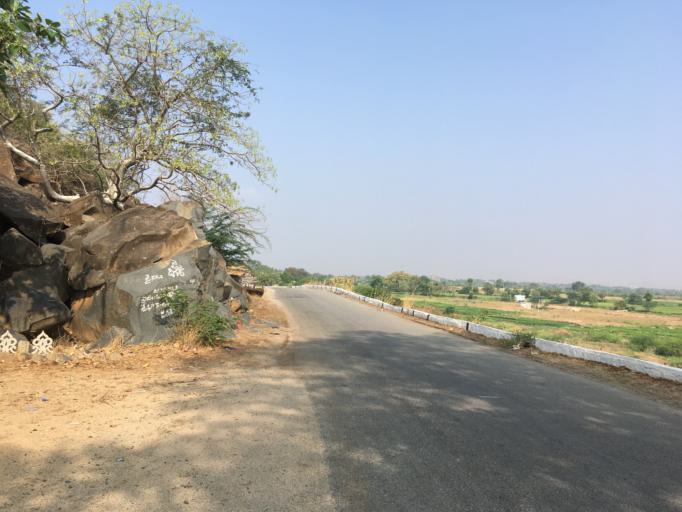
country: IN
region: Andhra Pradesh
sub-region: Anantapur
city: Puttaparthi
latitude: 14.1856
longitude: 77.7807
